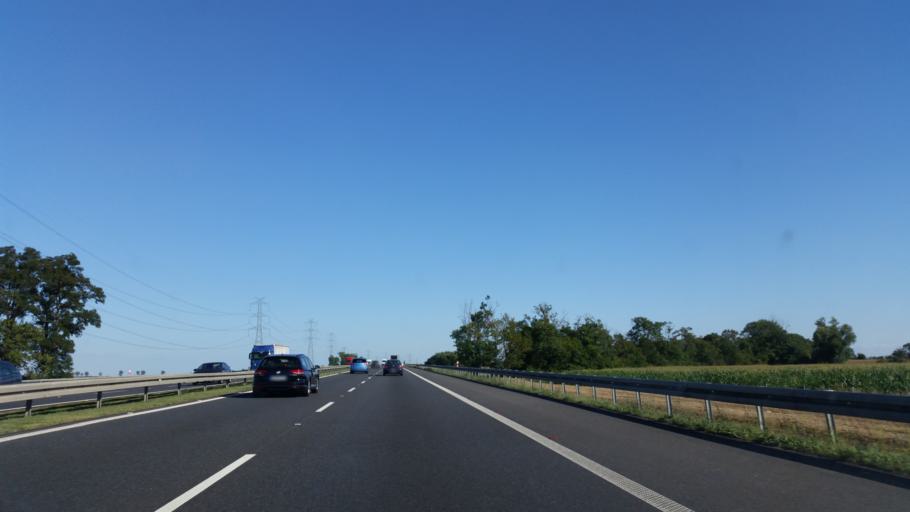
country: PL
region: Lower Silesian Voivodeship
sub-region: Powiat olawski
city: Wierzbno
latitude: 50.9067
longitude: 17.1593
